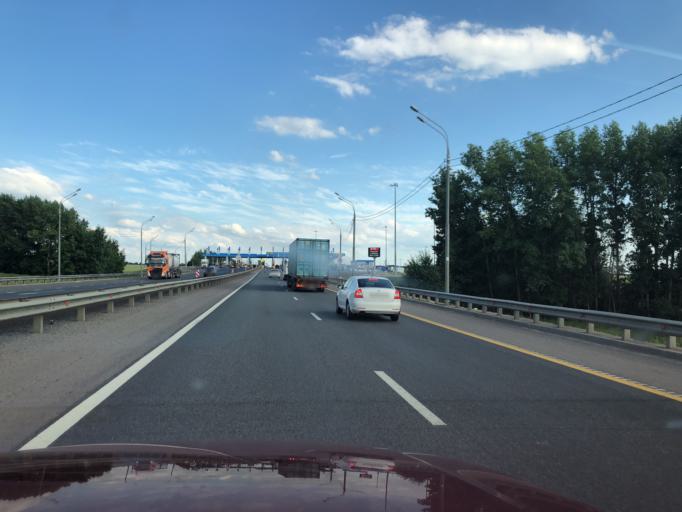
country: RU
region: Lipetsk
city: Zadonsk
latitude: 52.4329
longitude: 38.8218
